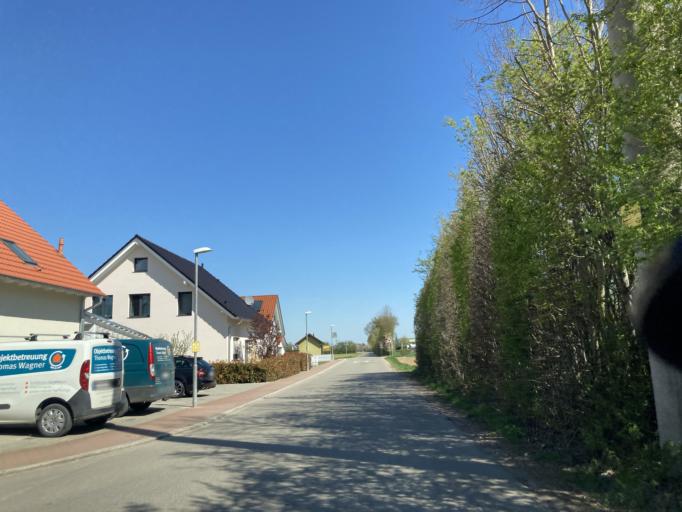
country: DE
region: Baden-Wuerttemberg
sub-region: Freiburg Region
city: Schliengen
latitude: 47.7717
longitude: 7.5585
